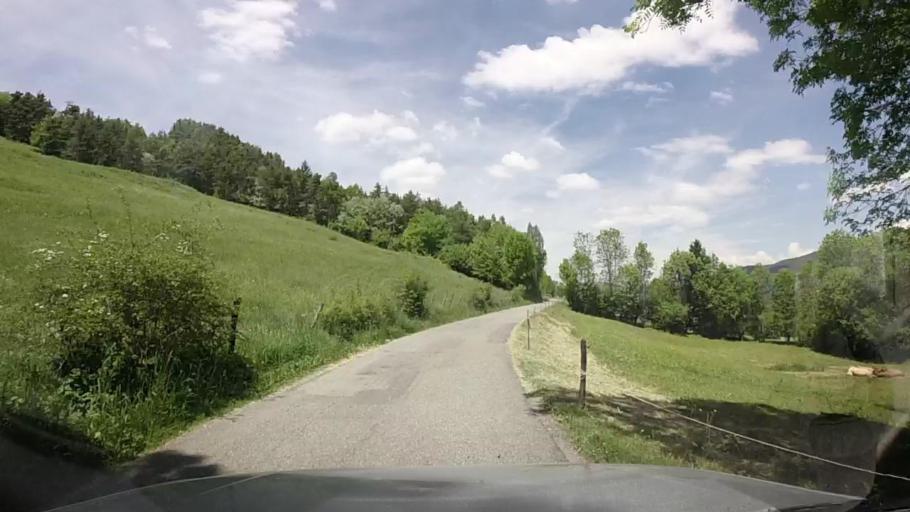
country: FR
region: Provence-Alpes-Cote d'Azur
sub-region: Departement des Alpes-de-Haute-Provence
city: Seyne-les-Alpes
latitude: 44.3321
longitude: 6.3495
